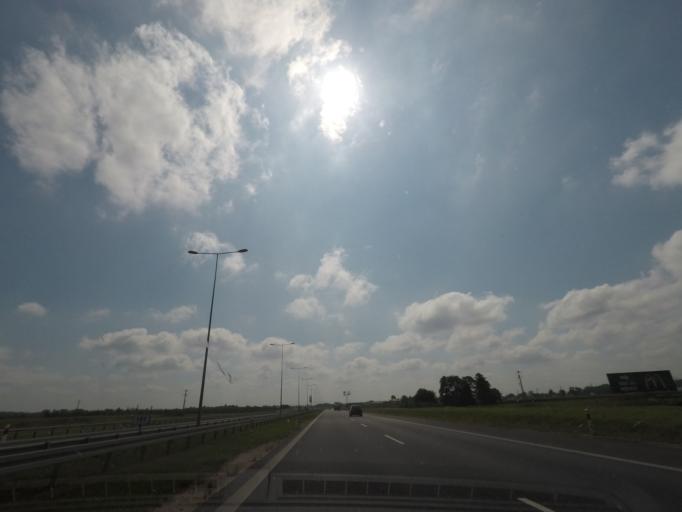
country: PL
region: Kujawsko-Pomorskie
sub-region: Powiat wloclawski
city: Brzesc Kujawski
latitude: 52.6600
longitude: 18.9210
